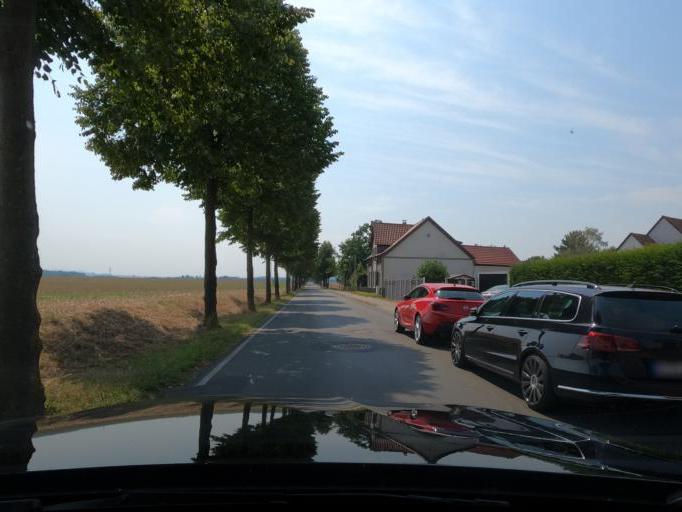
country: DE
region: Lower Saxony
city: Nordstemmen
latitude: 52.2135
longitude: 9.7934
